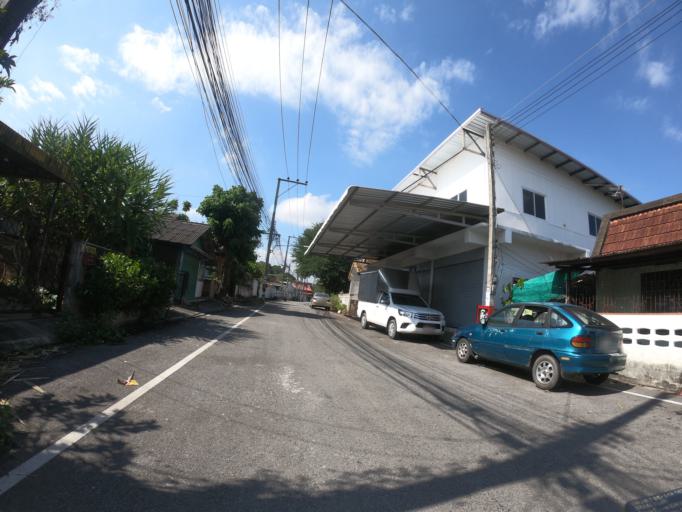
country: TH
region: Chiang Mai
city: Chiang Mai
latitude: 18.7432
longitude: 98.9562
